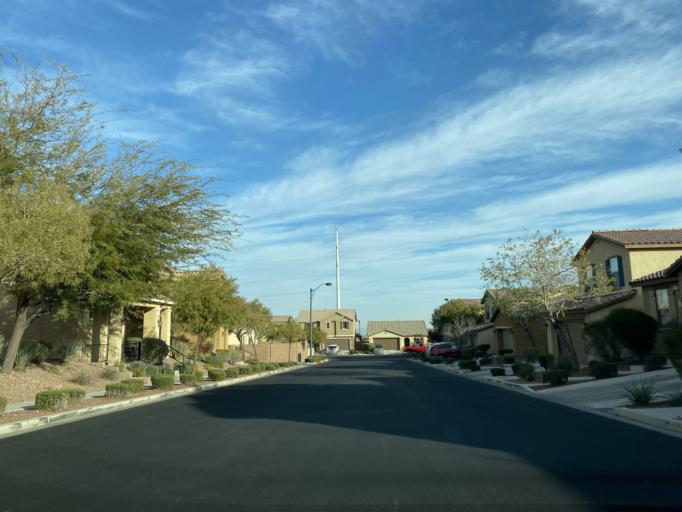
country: US
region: Nevada
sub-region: Clark County
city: Summerlin South
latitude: 36.2958
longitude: -115.3305
